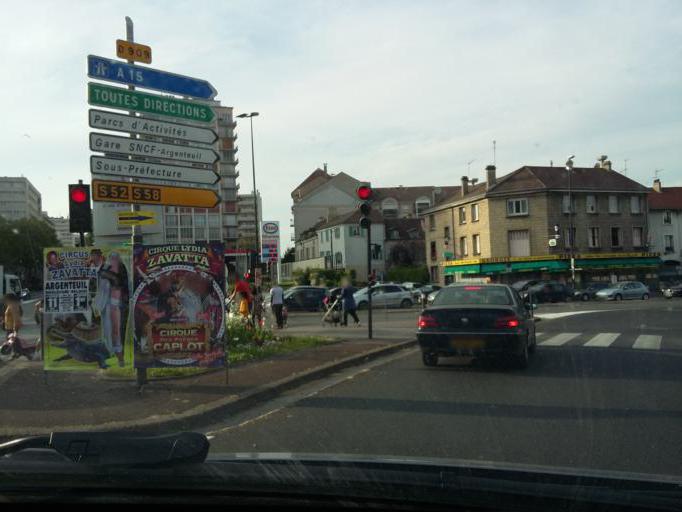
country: FR
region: Ile-de-France
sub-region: Departement du Val-d'Oise
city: Argenteuil
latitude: 48.9420
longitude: 2.2534
